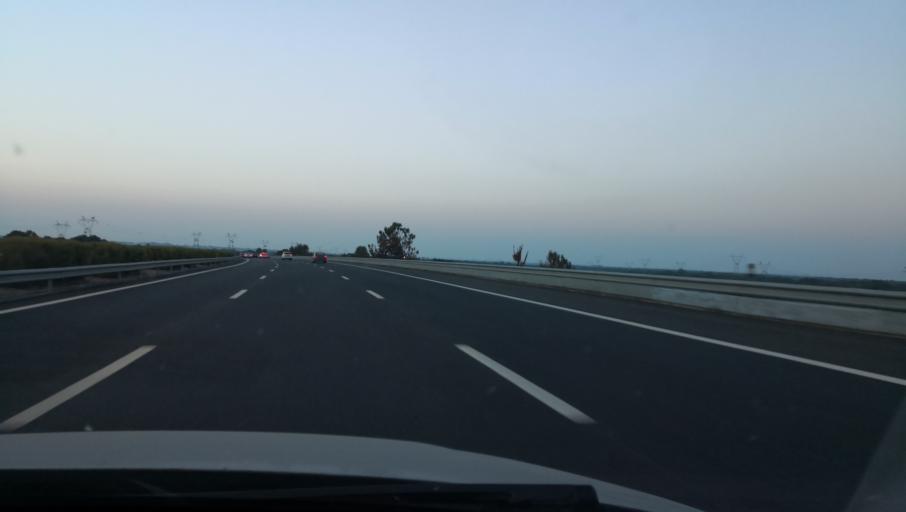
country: PT
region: Setubal
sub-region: Palmela
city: Pinhal Novo
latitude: 38.6316
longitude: -8.8667
